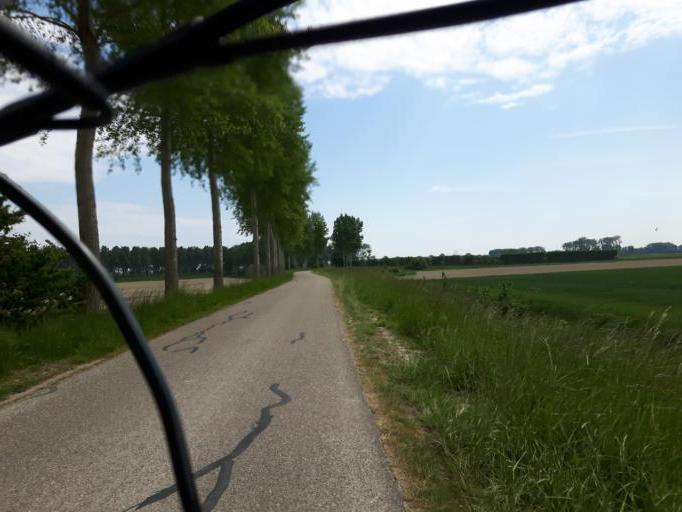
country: NL
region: Zeeland
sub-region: Gemeente Goes
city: Goes
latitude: 51.4481
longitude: 3.8250
